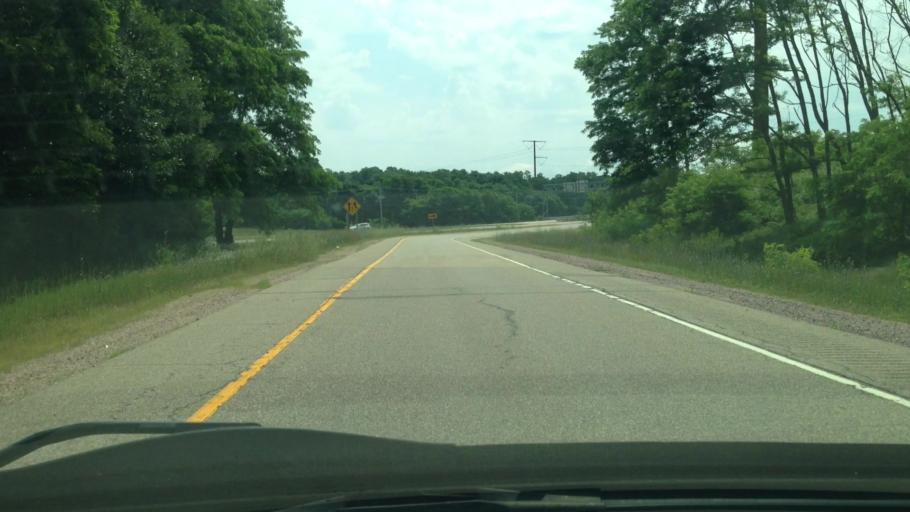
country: US
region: Wisconsin
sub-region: Sauk County
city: Lake Delton
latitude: 43.5680
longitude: -89.7802
